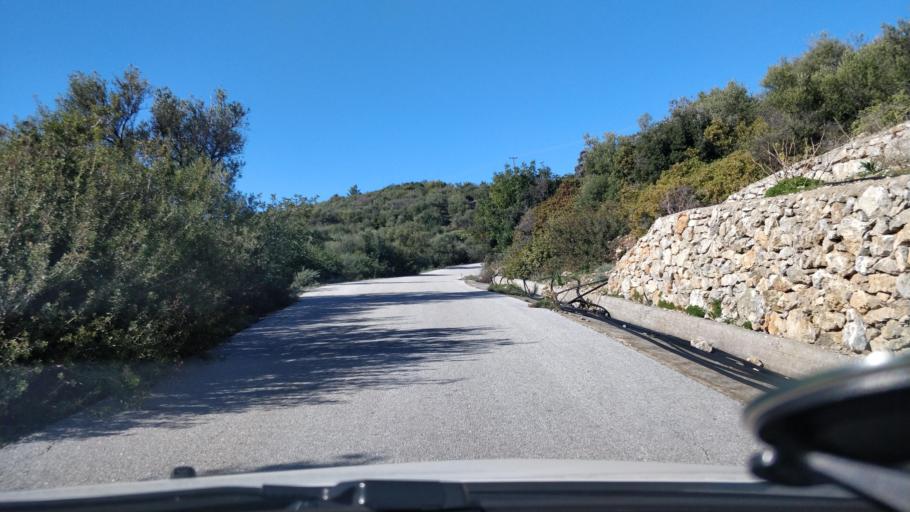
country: GR
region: Crete
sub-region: Nomos Lasithiou
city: Gra Liyia
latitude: 35.0187
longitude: 25.5517
